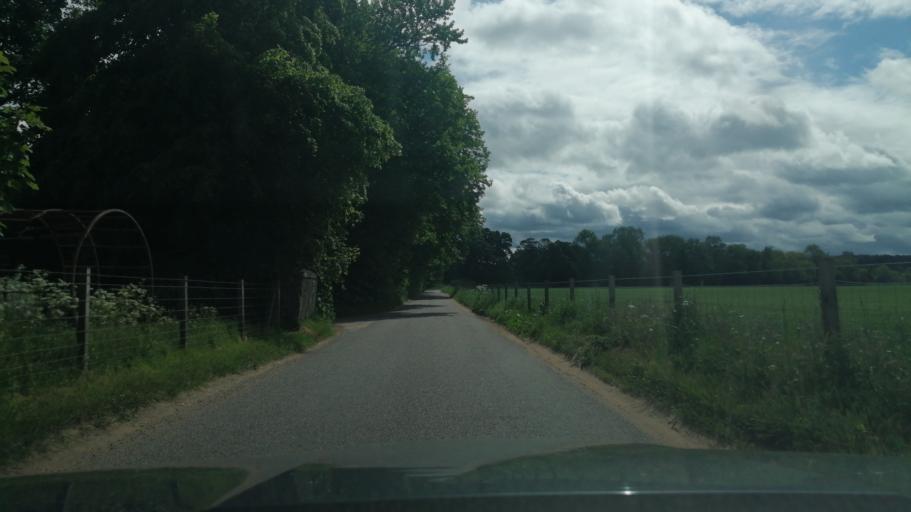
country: GB
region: Scotland
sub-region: Moray
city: Lhanbryd
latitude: 57.6570
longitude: -3.2544
